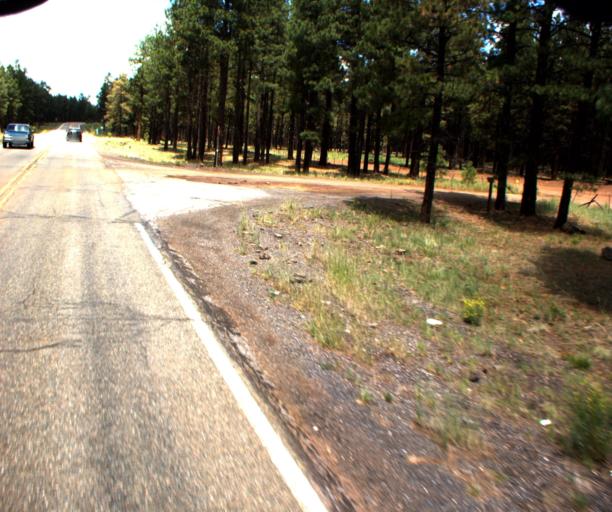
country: US
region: Arizona
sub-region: Coconino County
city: Parks
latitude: 35.3492
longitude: -111.7901
